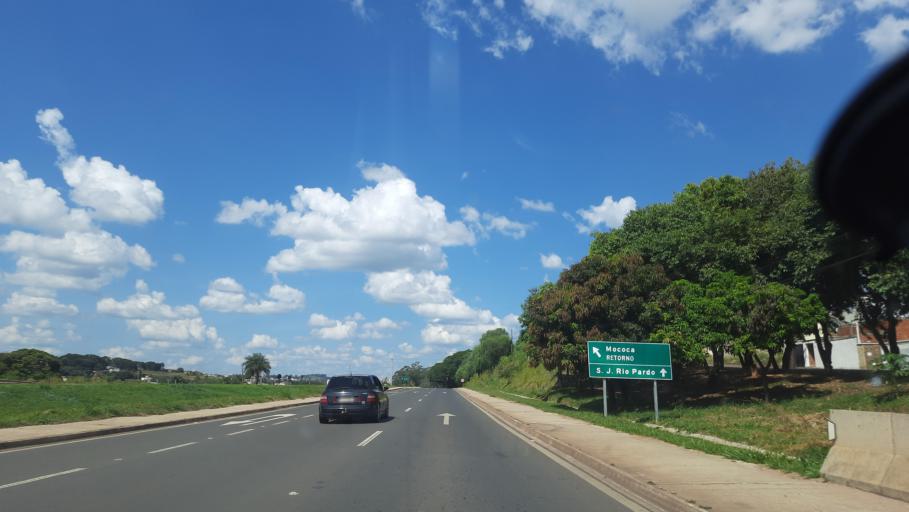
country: BR
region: Sao Paulo
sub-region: Sao Jose Do Rio Pardo
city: Sao Jose do Rio Pardo
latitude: -21.6023
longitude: -46.9102
